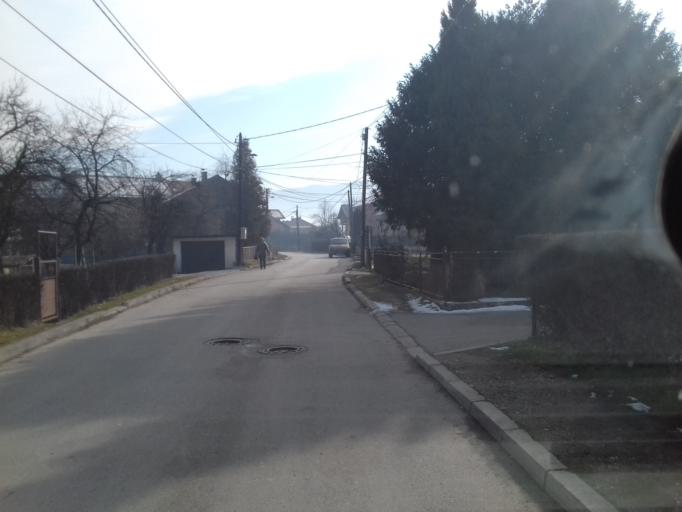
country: BA
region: Federation of Bosnia and Herzegovina
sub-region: Kanton Sarajevo
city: Sarajevo
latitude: 43.8156
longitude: 18.3109
